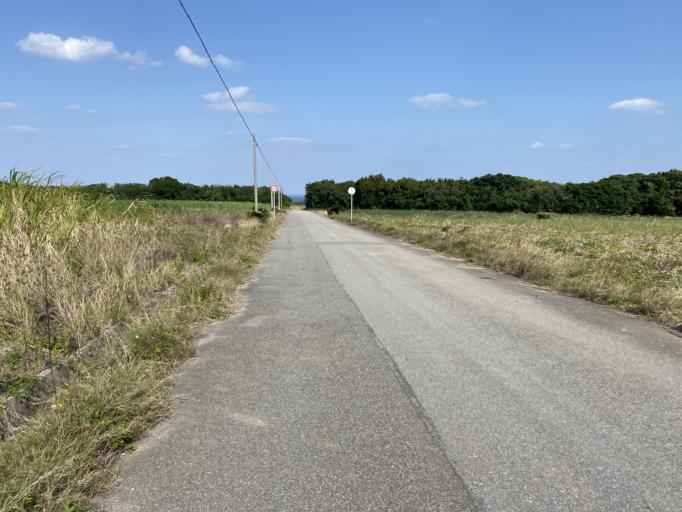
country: JP
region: Okinawa
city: Ishigaki
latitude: 24.0578
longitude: 123.7895
